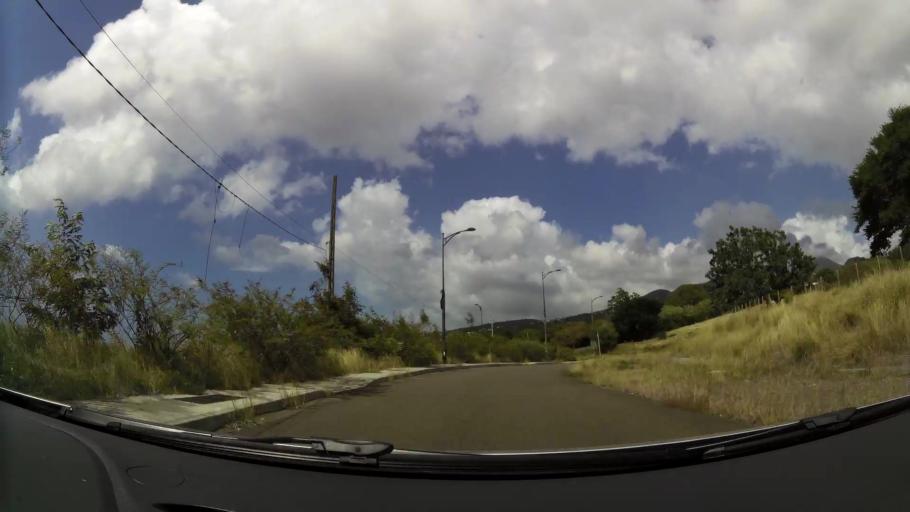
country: MQ
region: Martinique
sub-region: Martinique
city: Fort-de-France
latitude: 14.6367
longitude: -61.1337
